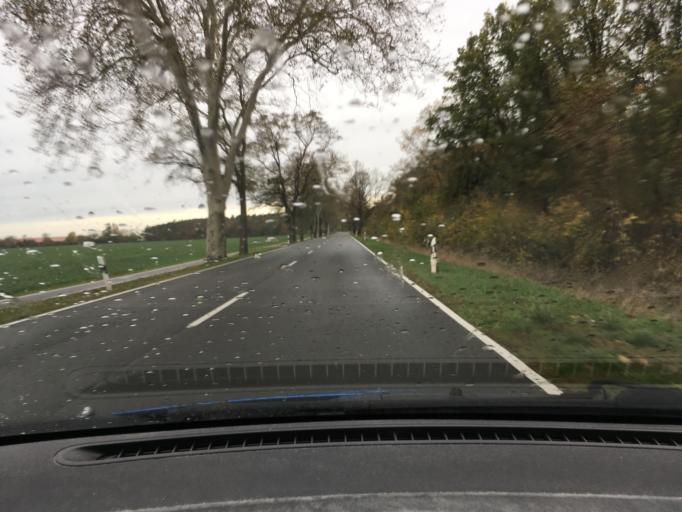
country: DE
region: Saxony-Anhalt
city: Rodleben
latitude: 51.9074
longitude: 12.2019
